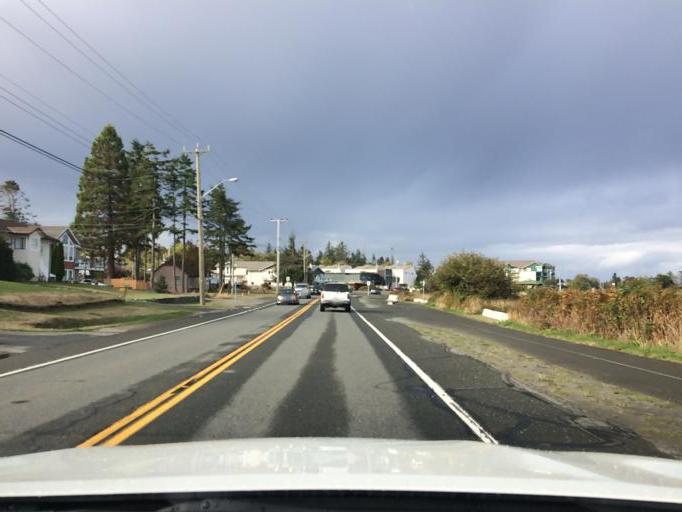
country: CA
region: British Columbia
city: Campbell River
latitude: 49.9608
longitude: -125.2085
